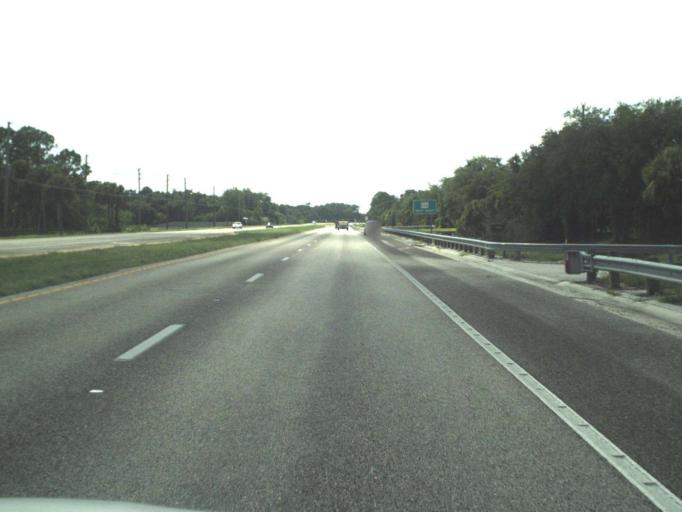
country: US
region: Florida
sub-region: Brevard County
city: Cocoa West
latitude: 28.3599
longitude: -80.8171
